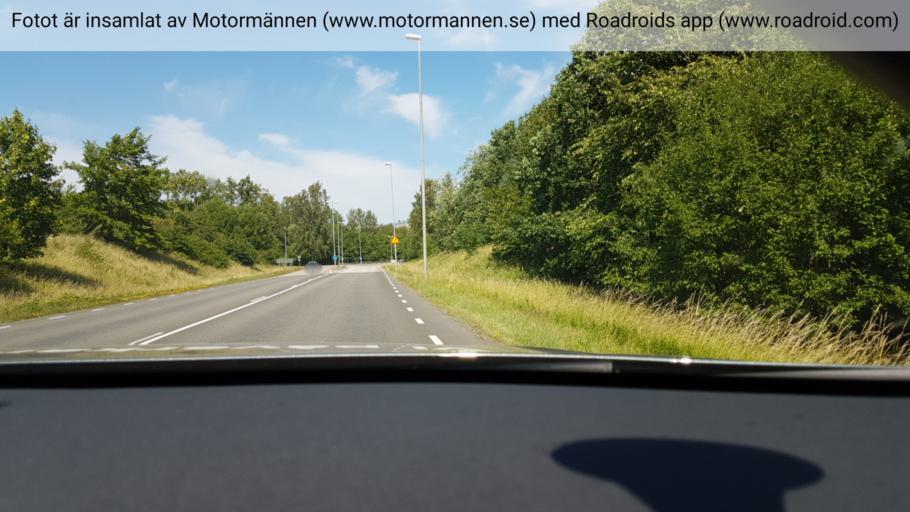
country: SE
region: Vaestra Goetaland
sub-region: Skovde Kommun
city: Skoevde
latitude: 58.4217
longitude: 13.8476
